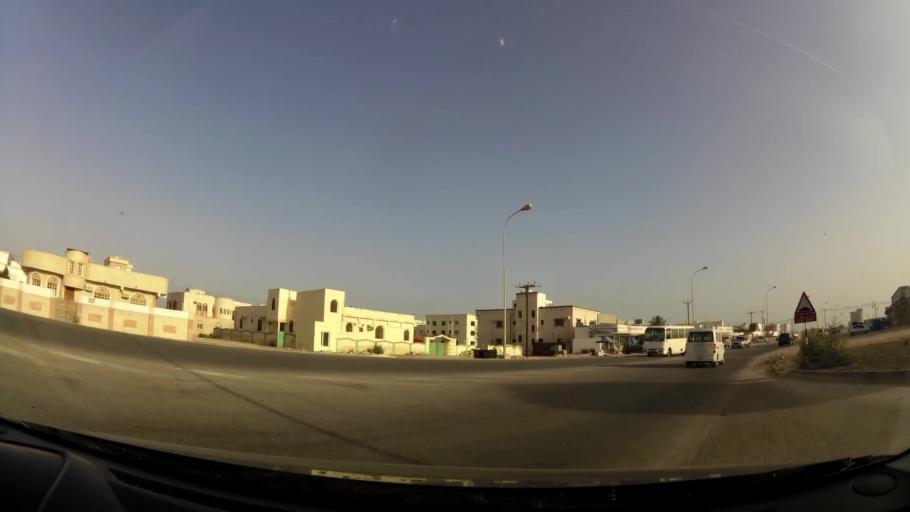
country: OM
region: Zufar
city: Salalah
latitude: 17.0021
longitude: 54.0321
